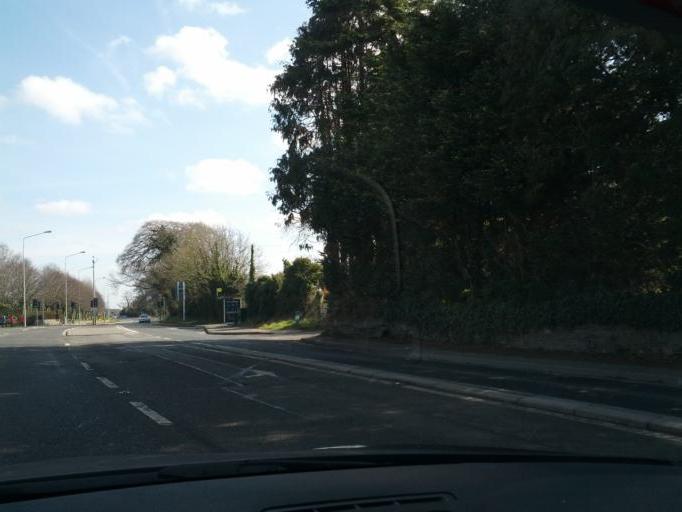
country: IE
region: Leinster
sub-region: Kildare
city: Leixlip
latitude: 53.3746
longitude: -6.5292
